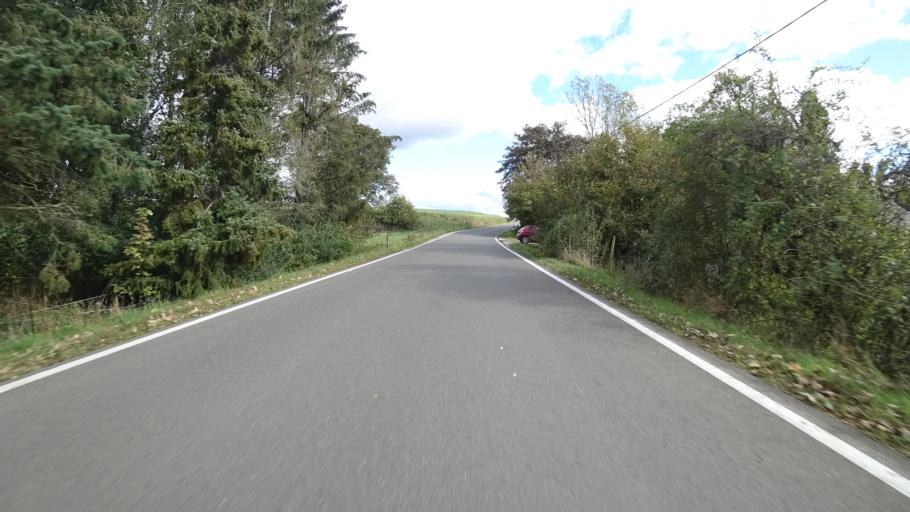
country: DE
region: Rheinland-Pfalz
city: Rayerschied
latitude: 50.0173
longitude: 7.5872
